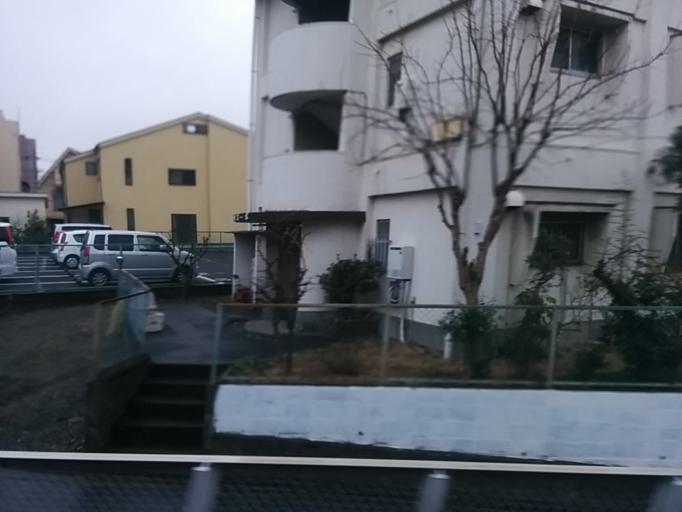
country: JP
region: Tokyo
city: Kokubunji
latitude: 35.6713
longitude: 139.4696
